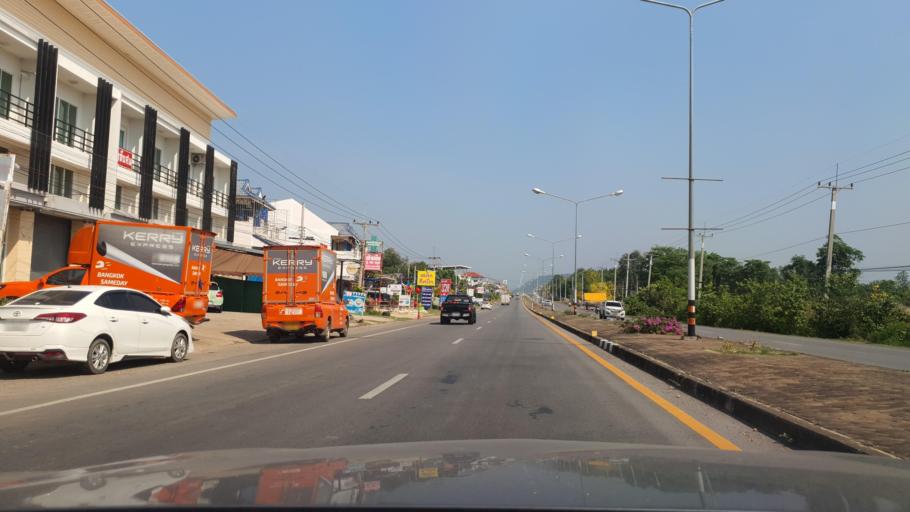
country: TH
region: Kanchanaburi
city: Kanchanaburi
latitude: 14.0859
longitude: 99.4290
